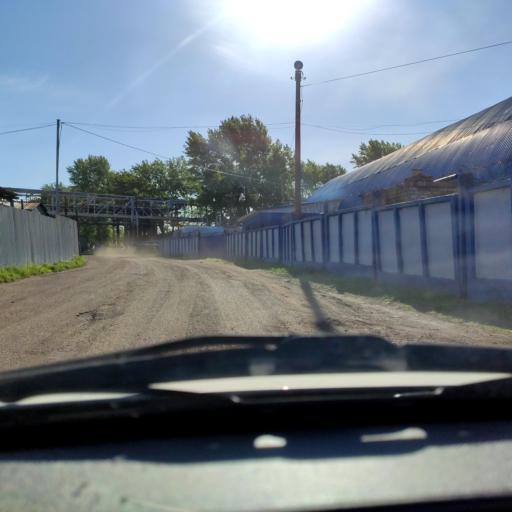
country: RU
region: Bashkortostan
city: Ufa
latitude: 54.8588
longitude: 56.0872
